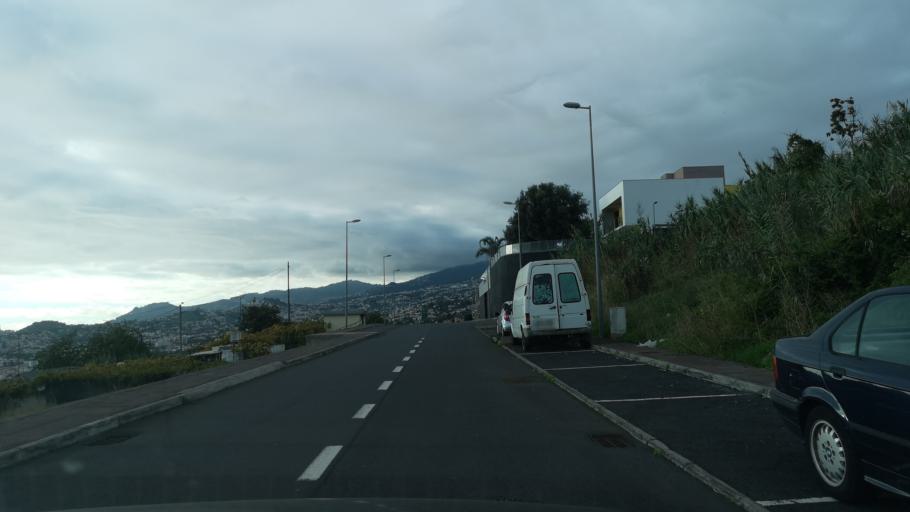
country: PT
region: Madeira
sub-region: Funchal
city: Nossa Senhora do Monte
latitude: 32.6550
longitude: -16.8903
